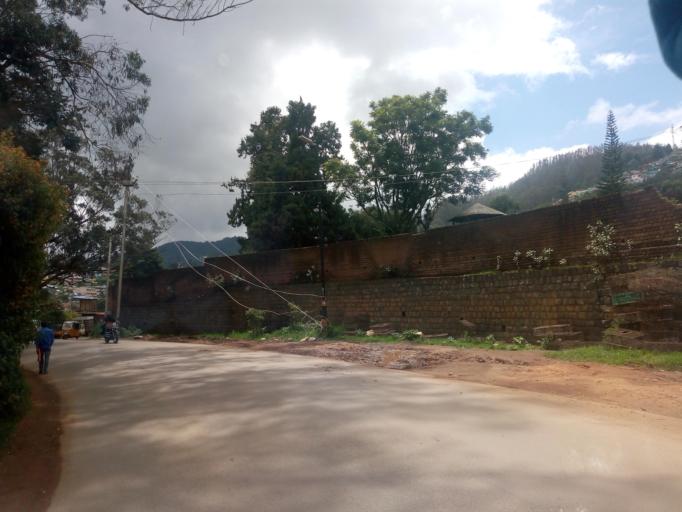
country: IN
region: Tamil Nadu
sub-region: Nilgiri
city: Ooty
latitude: 11.4009
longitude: 76.7004
